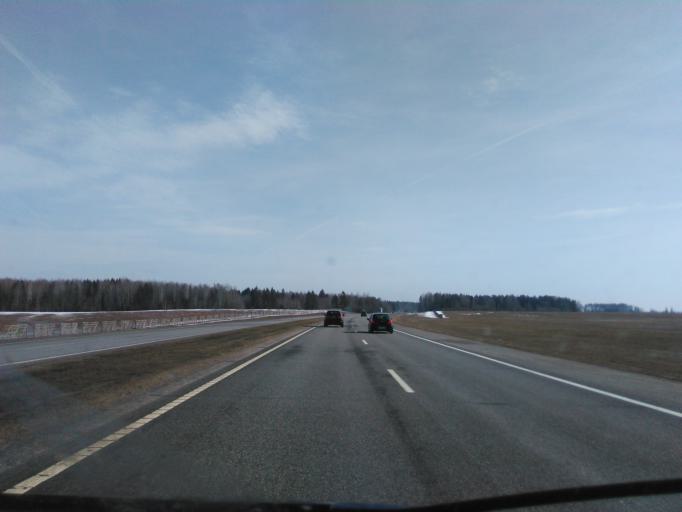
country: BY
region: Vitebsk
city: Talachyn
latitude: 54.4795
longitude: 29.8326
